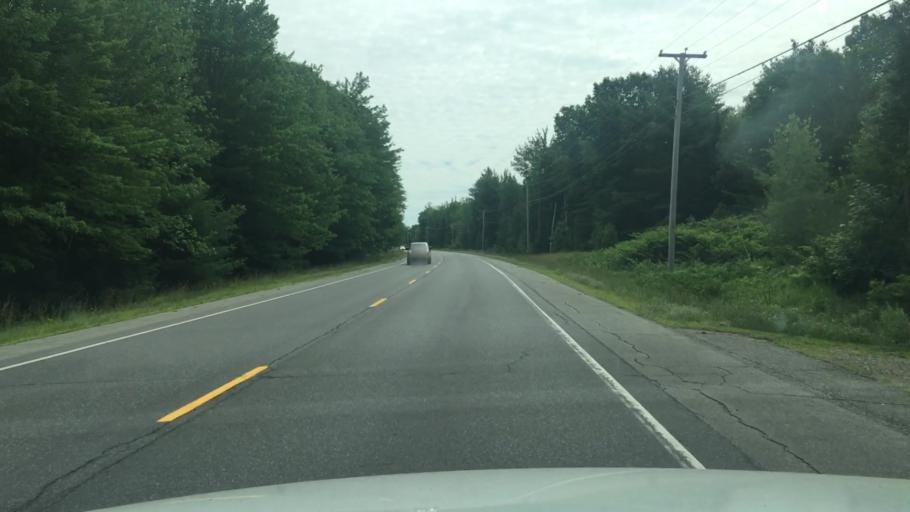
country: US
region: Maine
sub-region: Waldo County
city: Burnham
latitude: 44.6131
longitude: -69.3646
